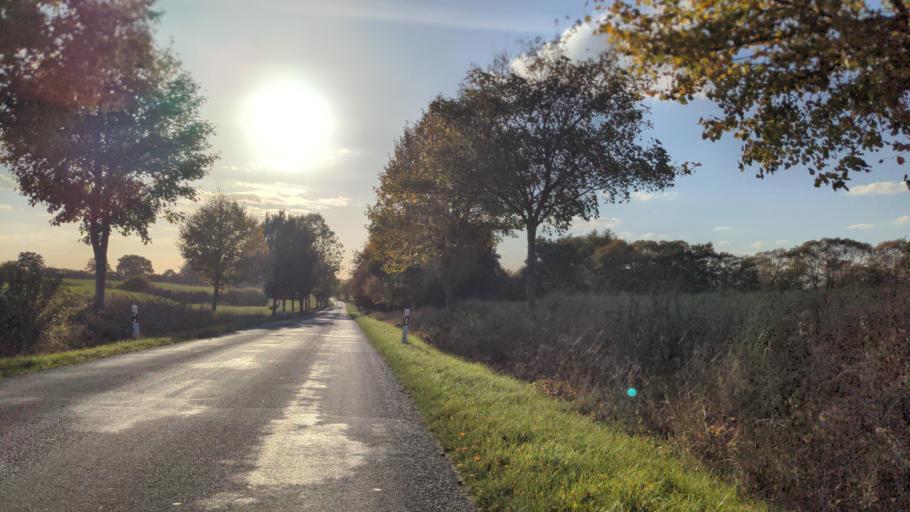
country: DE
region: Schleswig-Holstein
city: Pronstorf
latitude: 53.9606
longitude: 10.4909
